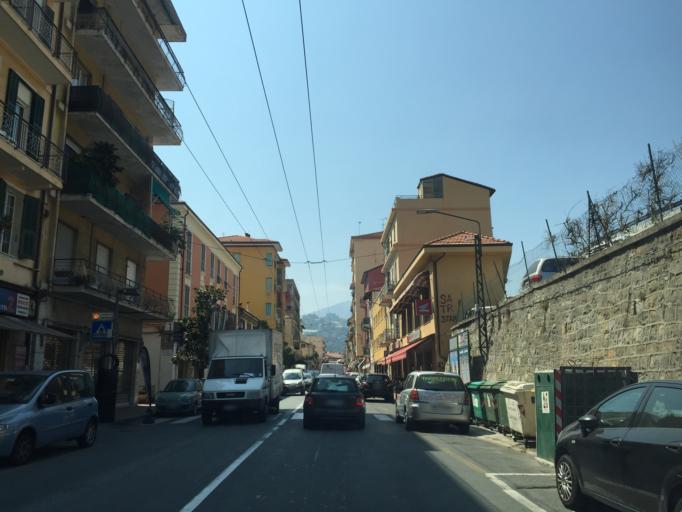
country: IT
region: Liguria
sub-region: Provincia di Imperia
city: Ventimiglia
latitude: 43.7902
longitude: 7.6145
